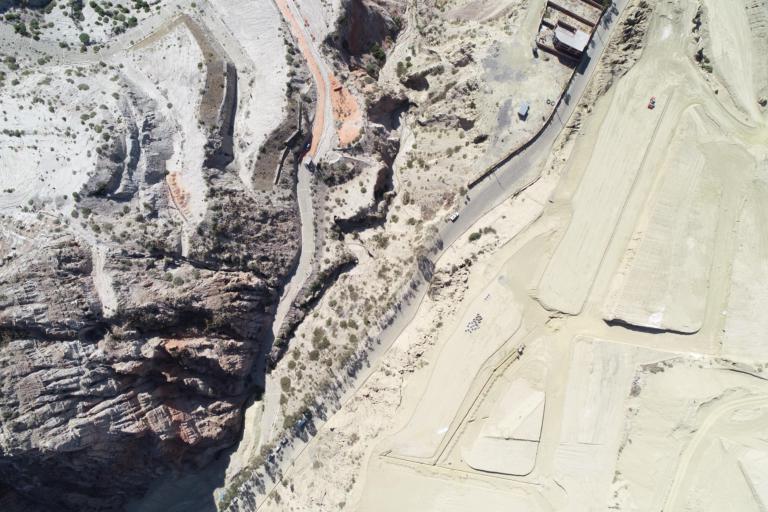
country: BO
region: La Paz
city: La Paz
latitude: -16.5572
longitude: -68.1084
